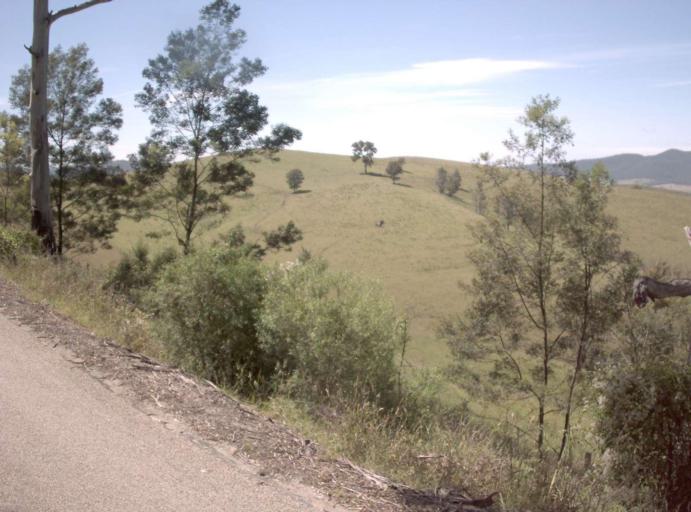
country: AU
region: Victoria
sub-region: East Gippsland
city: Lakes Entrance
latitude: -37.4643
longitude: 148.1924
